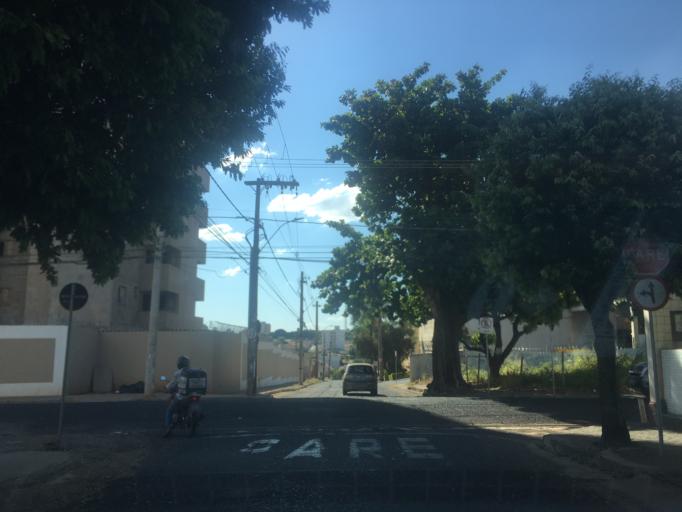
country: BR
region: Minas Gerais
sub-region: Uberlandia
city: Uberlandia
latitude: -18.9066
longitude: -48.2810
